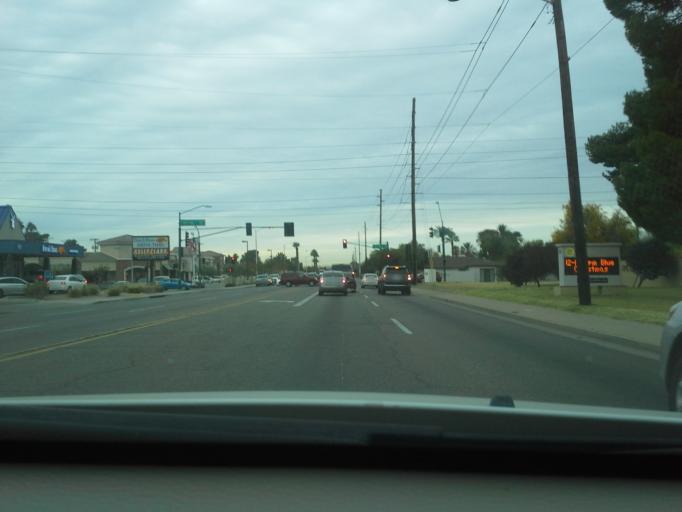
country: US
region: Arizona
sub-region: Maricopa County
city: Phoenix
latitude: 33.5383
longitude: -112.0554
